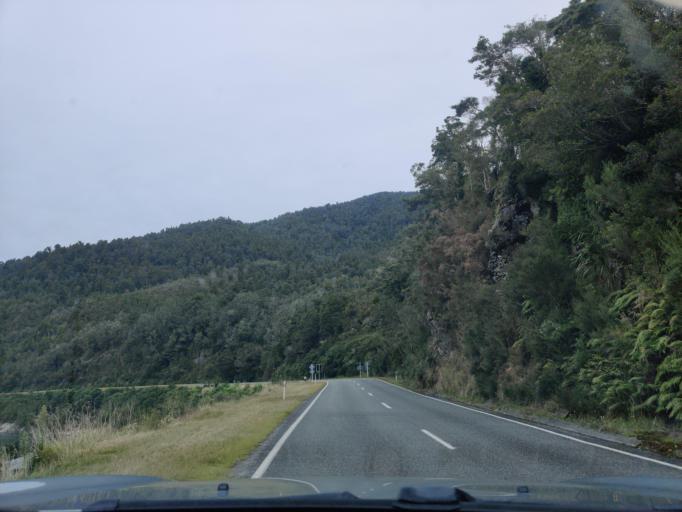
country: NZ
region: West Coast
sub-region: Buller District
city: Westport
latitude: -41.8466
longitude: 171.7149
